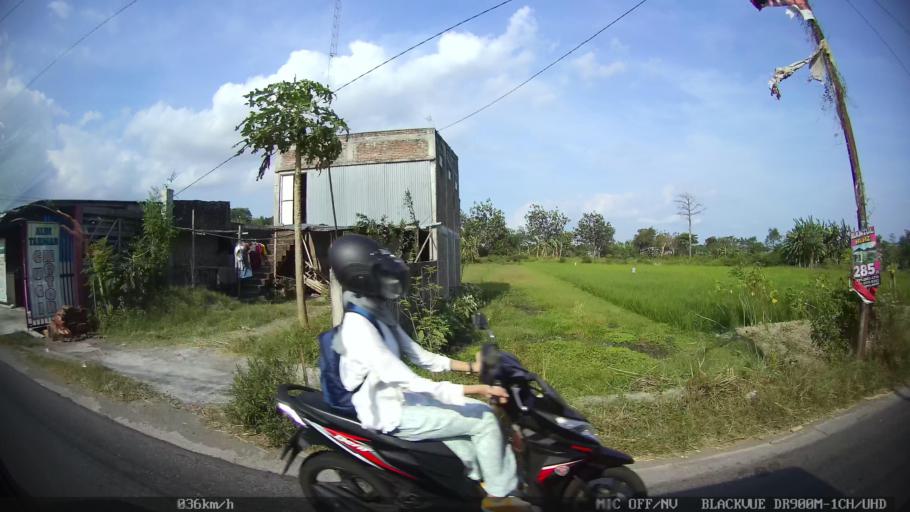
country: ID
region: Daerah Istimewa Yogyakarta
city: Kasihan
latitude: -7.8364
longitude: 110.3440
